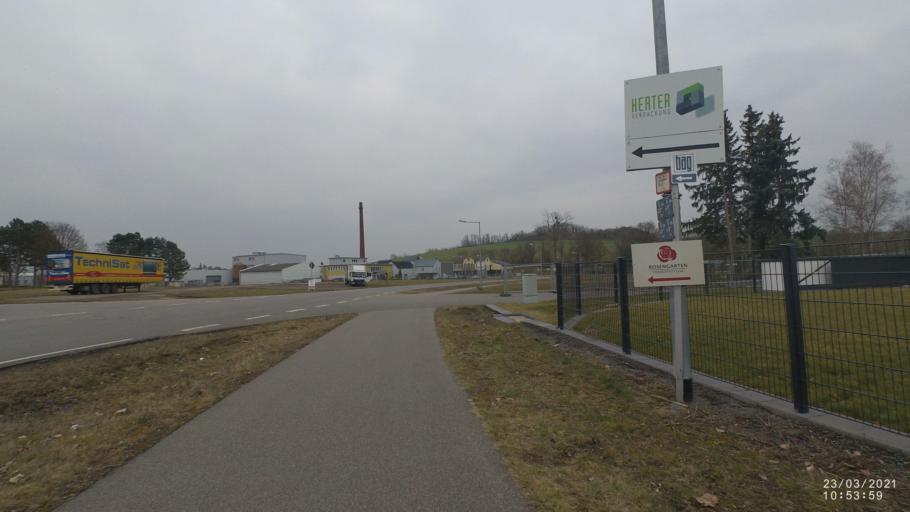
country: DE
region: Rheinland-Pfalz
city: Mendig
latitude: 50.3592
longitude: 7.3046
